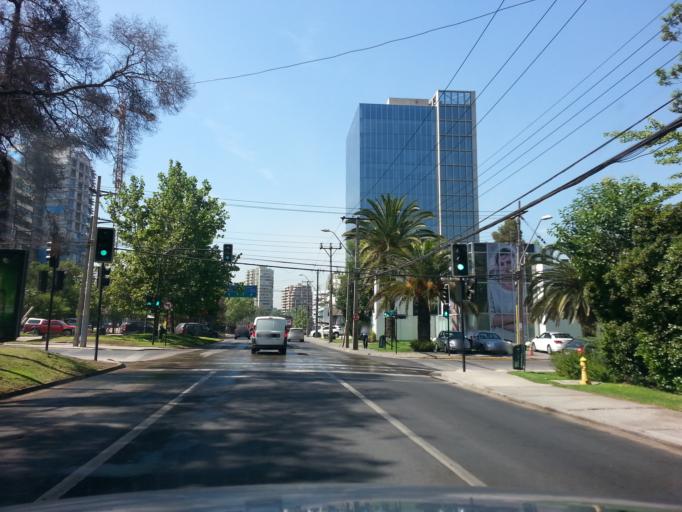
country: CL
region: Santiago Metropolitan
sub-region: Provincia de Santiago
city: Villa Presidente Frei, Nunoa, Santiago, Chile
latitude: -33.4017
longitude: -70.5872
